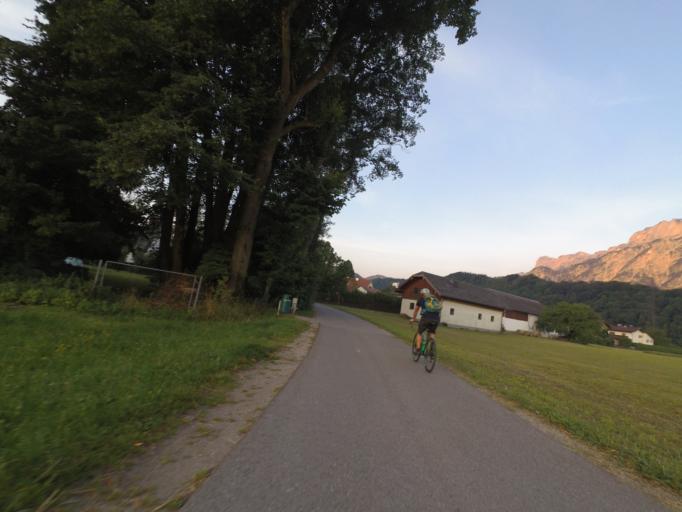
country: AT
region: Salzburg
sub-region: Politischer Bezirk Salzburg-Umgebung
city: Anif
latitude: 47.7324
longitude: 13.0600
